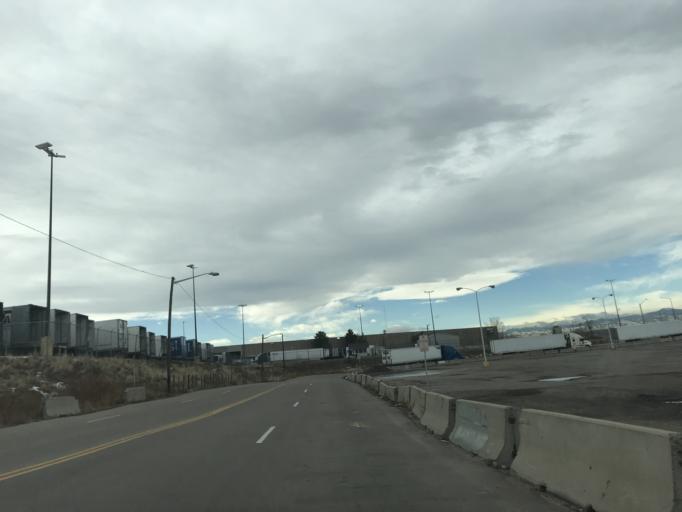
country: US
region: Colorado
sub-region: Denver County
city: Denver
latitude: 39.7773
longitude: -104.9735
